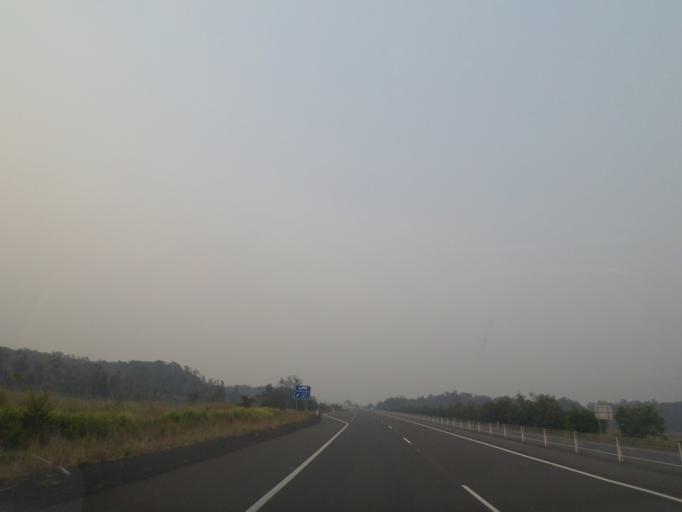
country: AU
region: New South Wales
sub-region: Nambucca Shire
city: Macksville
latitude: -30.7228
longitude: 152.9278
